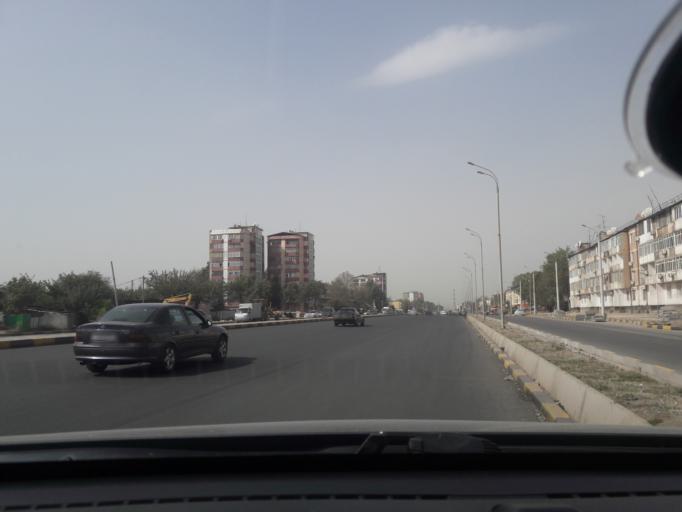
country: TJ
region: Dushanbe
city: Dushanbe
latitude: 38.5586
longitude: 68.7538
